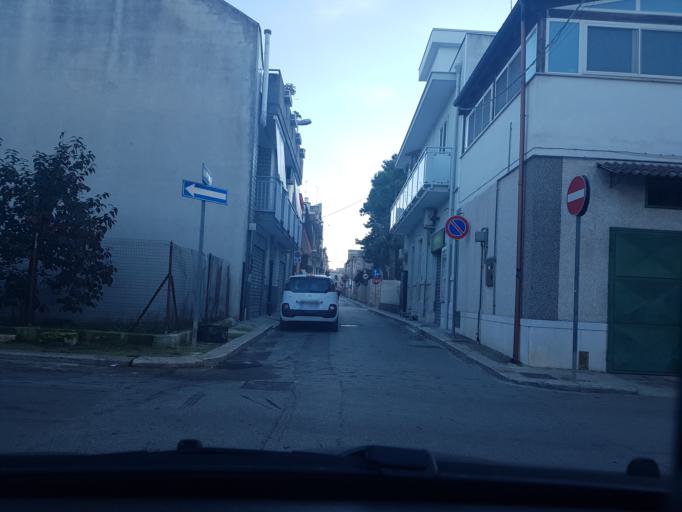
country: IT
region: Apulia
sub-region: Provincia di Bari
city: Bitritto
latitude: 41.0437
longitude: 16.8253
